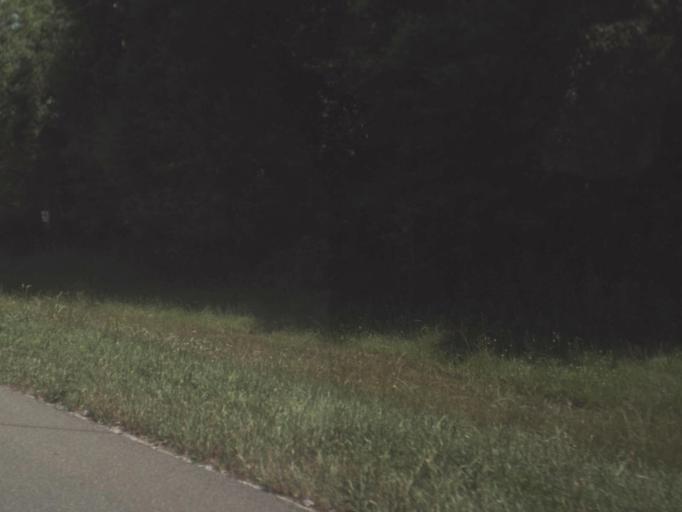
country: US
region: Florida
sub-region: Bradford County
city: Starke
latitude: 29.8909
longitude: -82.0850
